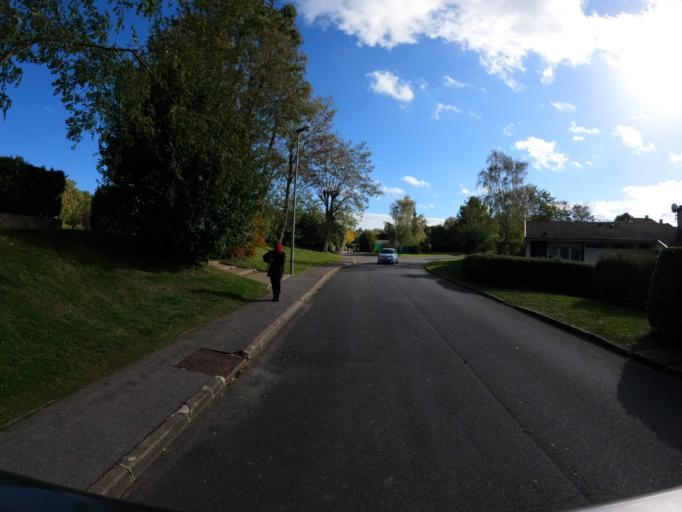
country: FR
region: Ile-de-France
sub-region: Departement de Seine-et-Marne
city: Esbly
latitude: 48.8914
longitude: 2.8106
